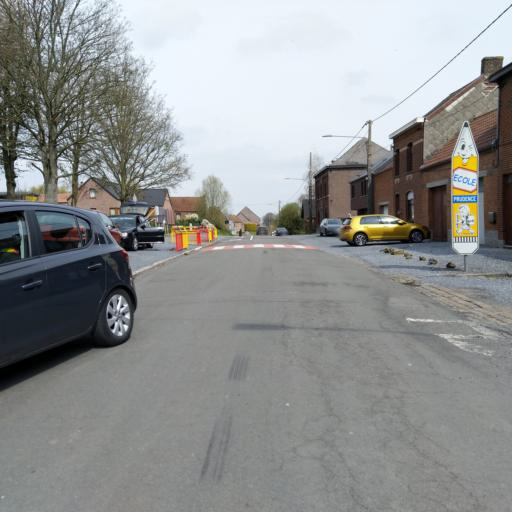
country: BE
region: Wallonia
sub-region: Province du Hainaut
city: Frameries
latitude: 50.3905
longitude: 3.9131
